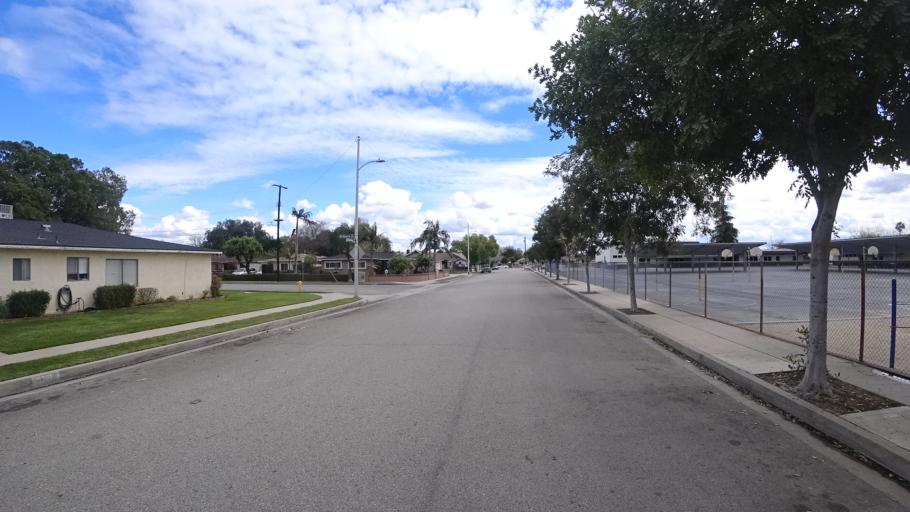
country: US
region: California
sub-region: Los Angeles County
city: Baldwin Park
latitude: 34.0807
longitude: -117.9613
